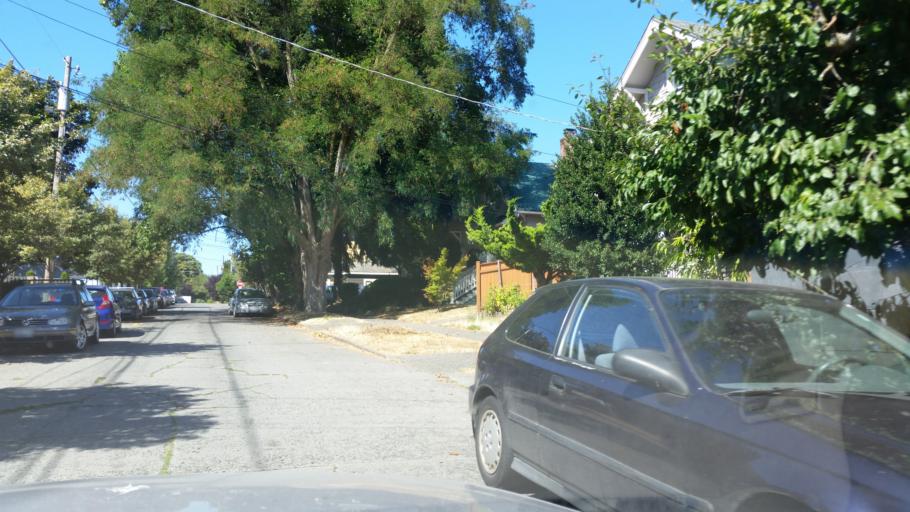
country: US
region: Washington
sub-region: King County
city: Seattle
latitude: 47.6604
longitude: -122.3273
